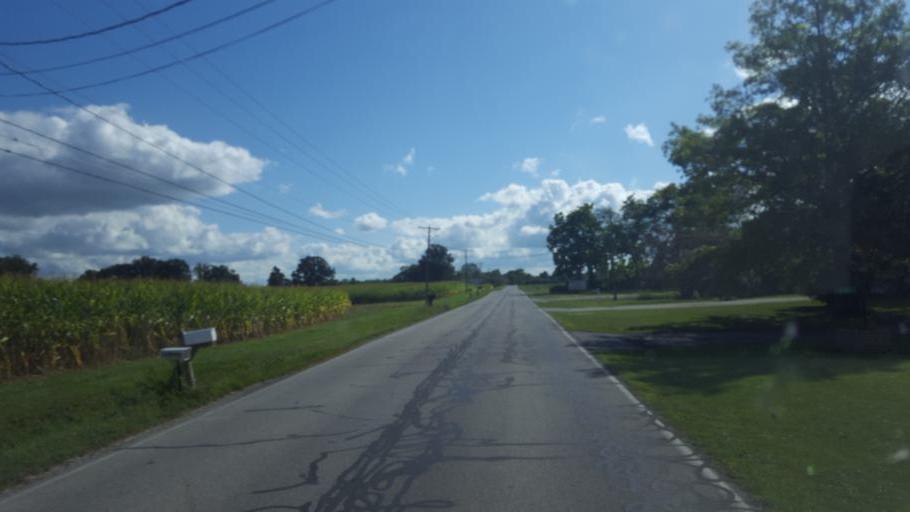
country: US
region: Ohio
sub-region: Lorain County
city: Oberlin
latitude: 41.2793
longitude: -82.1952
